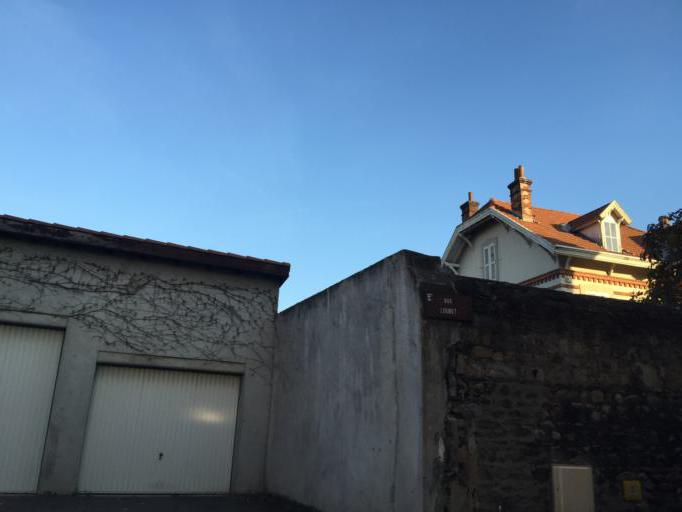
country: FR
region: Rhone-Alpes
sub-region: Departement de la Loire
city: Saint-Chamond
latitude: 45.4716
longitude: 4.5059
